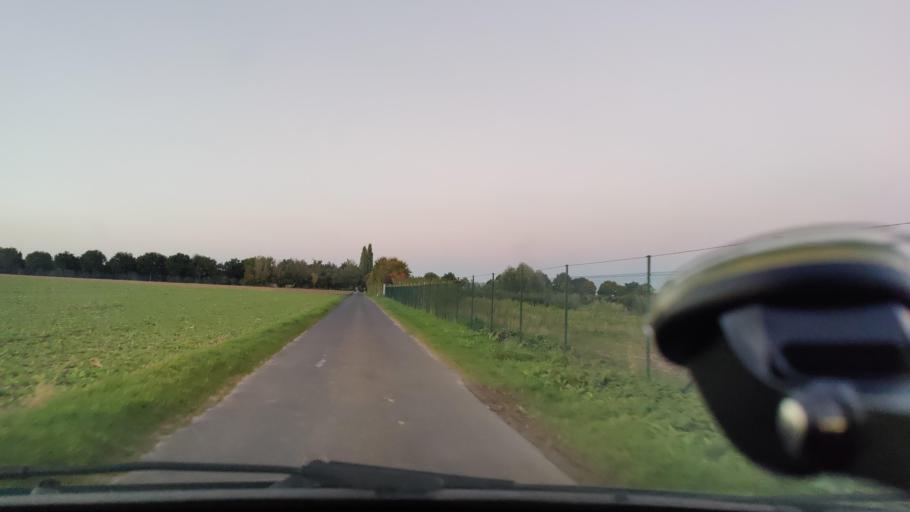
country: DE
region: North Rhine-Westphalia
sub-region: Regierungsbezirk Dusseldorf
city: Goch
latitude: 51.7158
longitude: 6.1799
